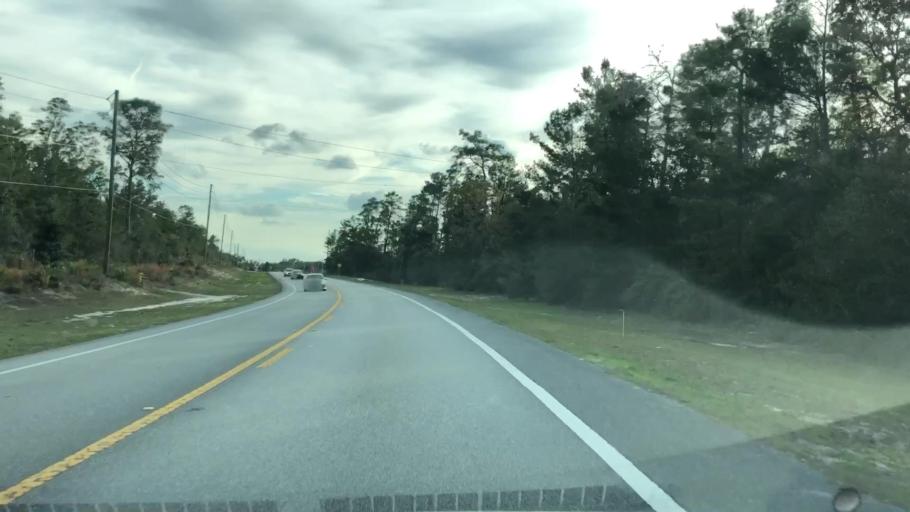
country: US
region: Florida
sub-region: Volusia County
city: Deltona
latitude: 28.9346
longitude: -81.2609
